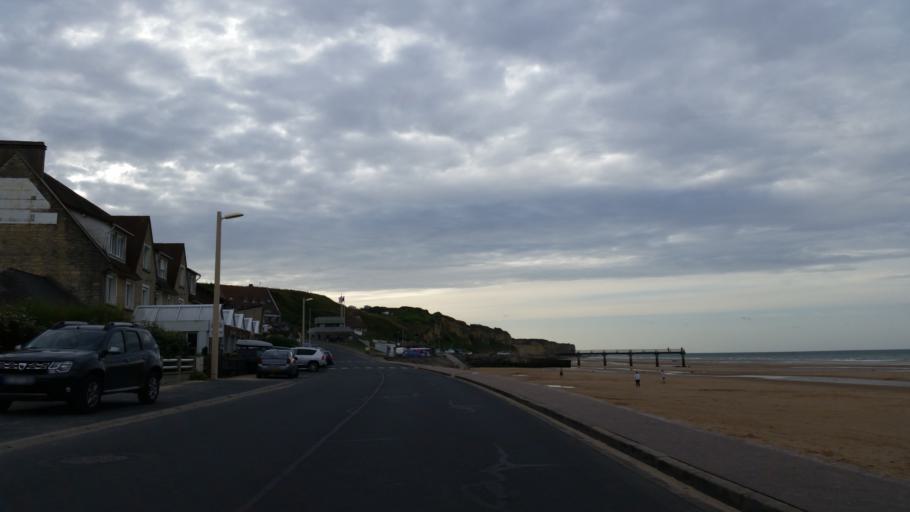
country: FR
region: Lower Normandy
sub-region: Departement du Calvados
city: Grandcamp-Maisy
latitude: 49.3785
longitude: -0.9006
